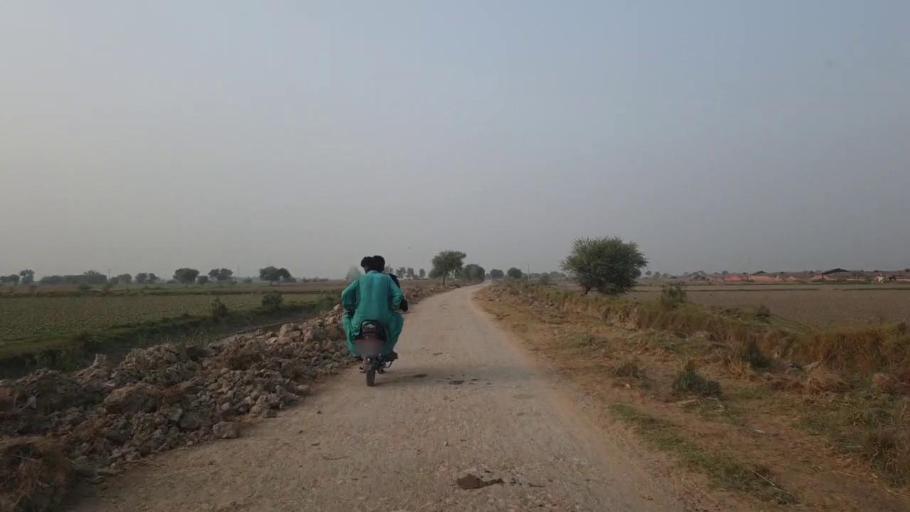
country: PK
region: Sindh
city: Mirpur Batoro
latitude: 24.6566
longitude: 68.3785
